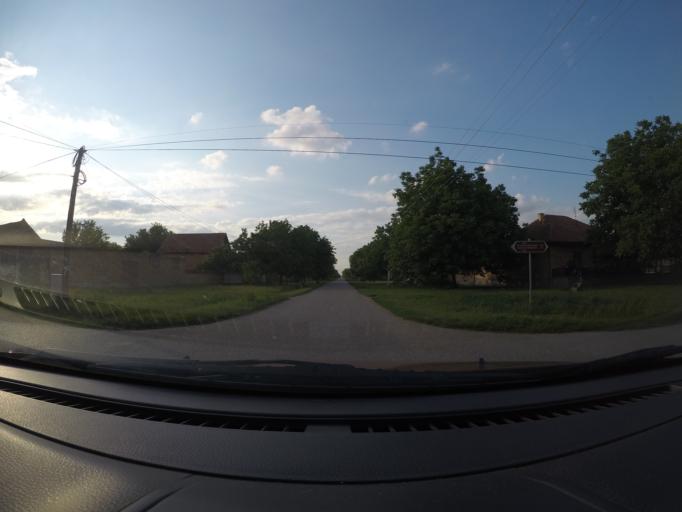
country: RS
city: Debeljaca
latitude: 45.0673
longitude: 20.6072
